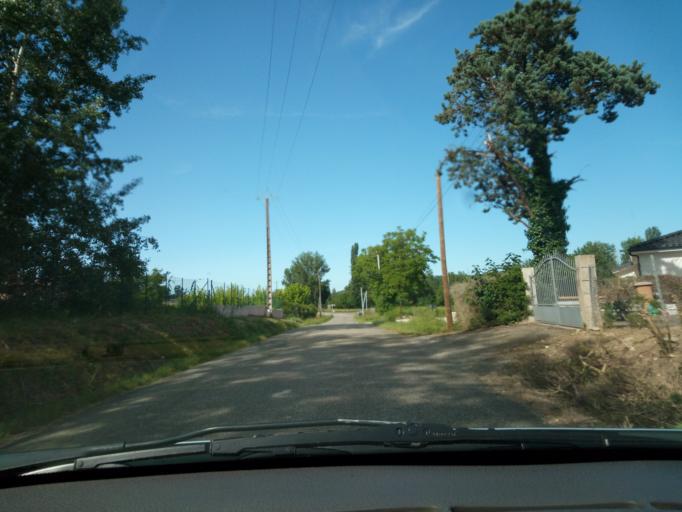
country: FR
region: Midi-Pyrenees
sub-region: Departement du Tarn-et-Garonne
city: Molieres
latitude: 44.2184
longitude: 1.3246
